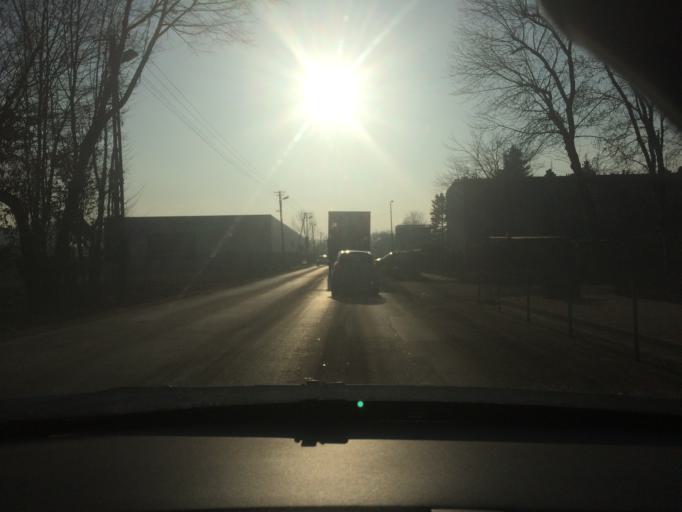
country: PL
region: Lesser Poland Voivodeship
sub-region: Powiat wielicki
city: Czarnochowice
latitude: 50.0262
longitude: 20.0386
